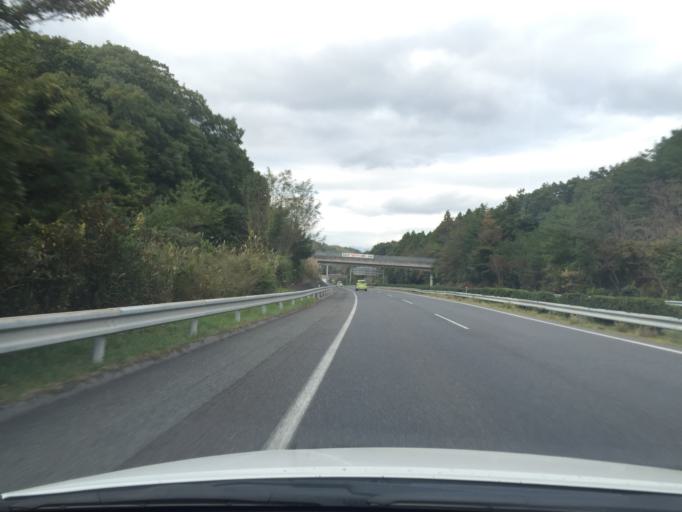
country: JP
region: Fukushima
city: Iwaki
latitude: 37.0424
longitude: 140.8201
